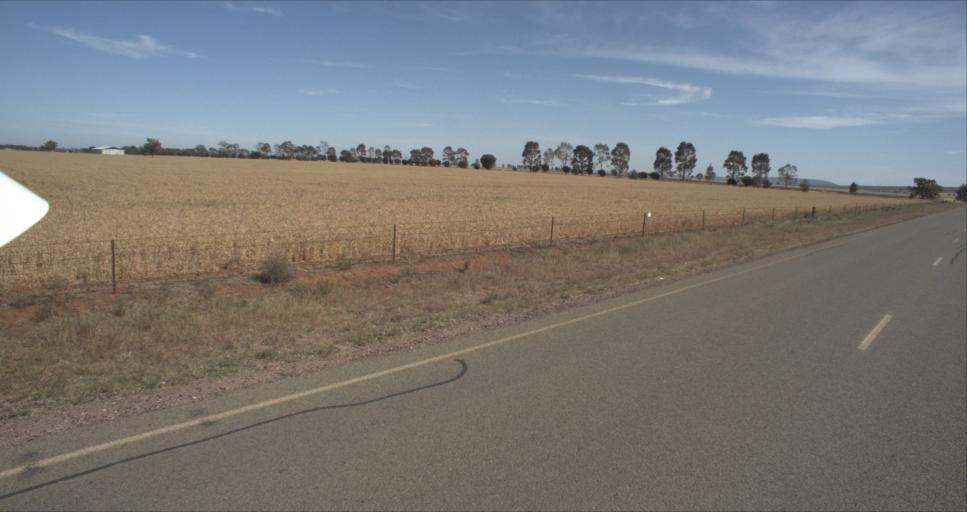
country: AU
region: New South Wales
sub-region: Leeton
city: Leeton
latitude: -34.5628
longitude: 146.4814
